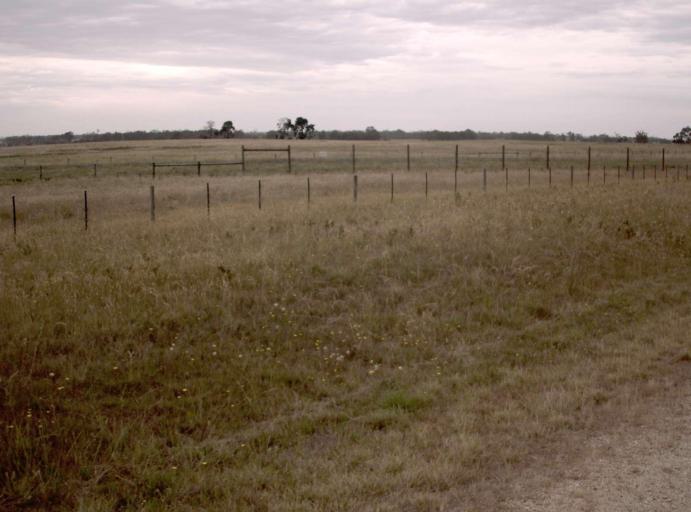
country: AU
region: Victoria
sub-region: Wellington
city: Sale
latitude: -38.1770
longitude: 147.2114
